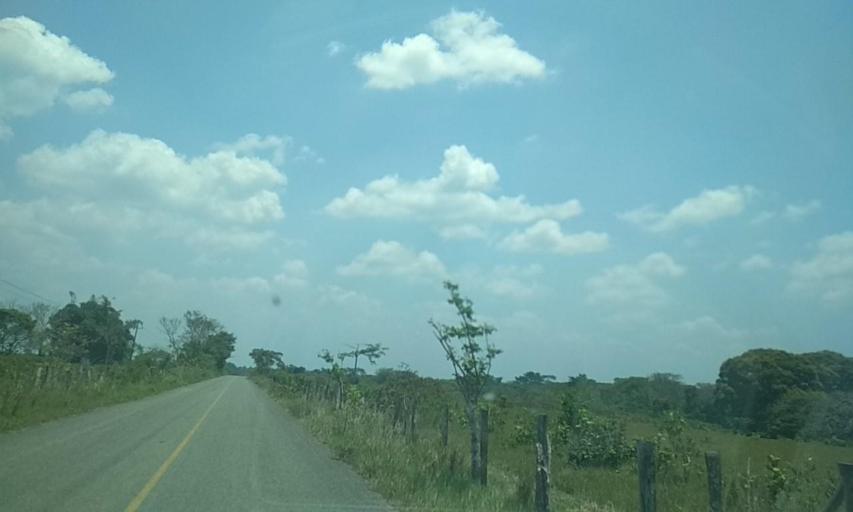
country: MX
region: Tabasco
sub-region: Huimanguillo
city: Francisco Rueda
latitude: 17.8259
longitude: -93.8721
